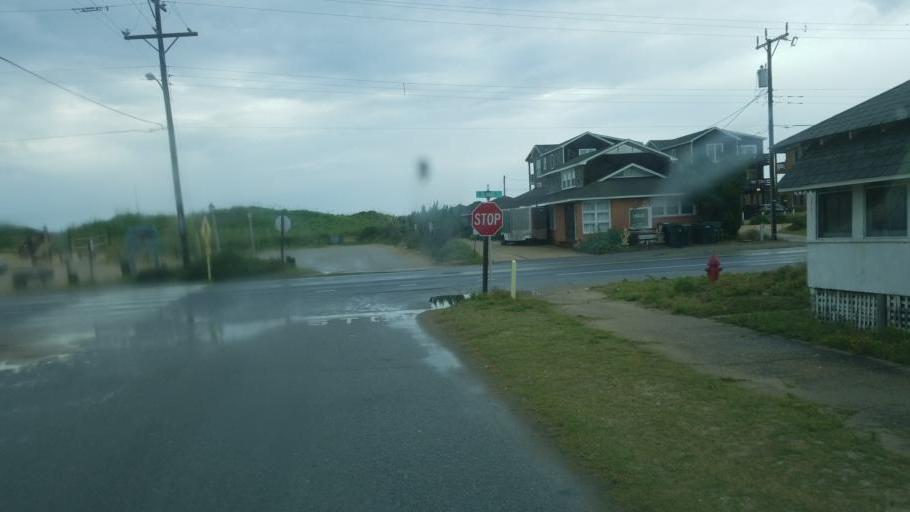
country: US
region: North Carolina
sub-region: Dare County
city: Nags Head
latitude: 35.9791
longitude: -75.6367
